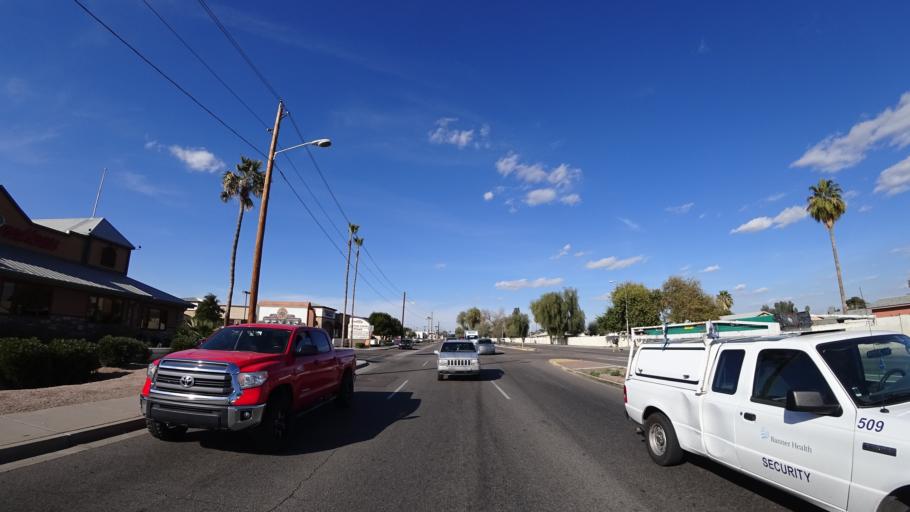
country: US
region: Arizona
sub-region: Maricopa County
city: Tolleson
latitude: 33.4673
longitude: -112.2207
